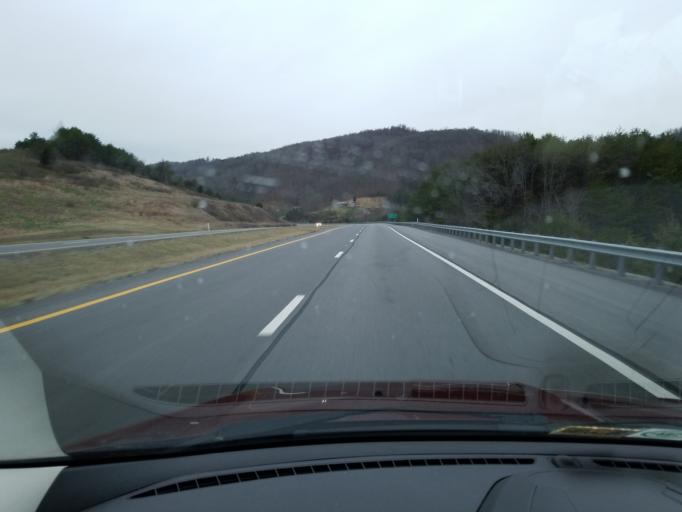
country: US
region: West Virginia
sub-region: Mercer County
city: Athens
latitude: 37.3421
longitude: -80.9791
